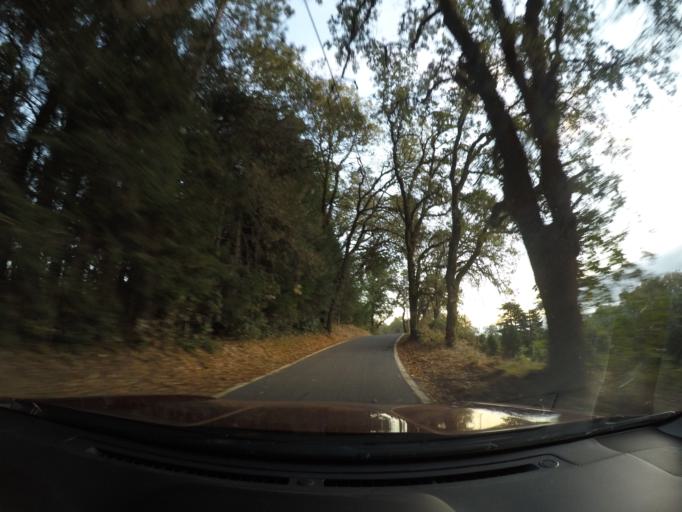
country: US
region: California
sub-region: Santa Clara County
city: Lexington Hills
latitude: 37.1818
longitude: -122.0307
